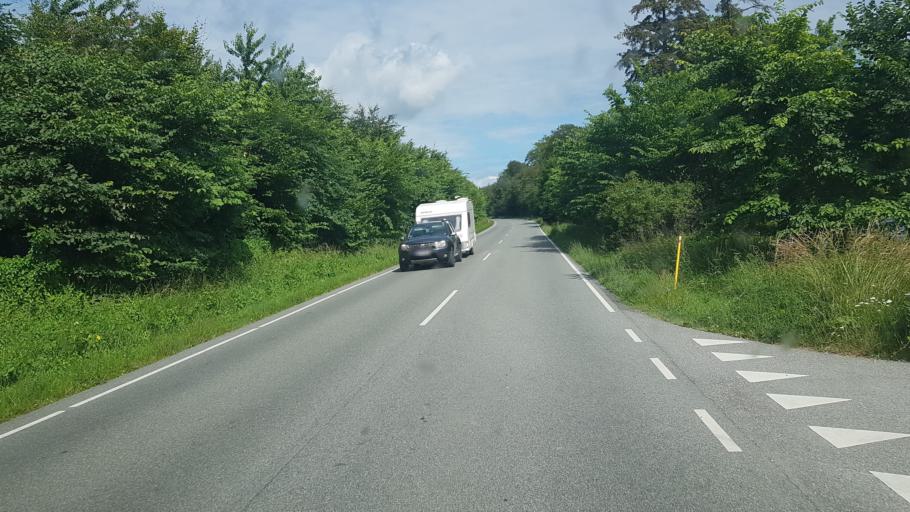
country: DK
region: South Denmark
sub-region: Kerteminde Kommune
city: Kerteminde
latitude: 55.4309
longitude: 10.6935
